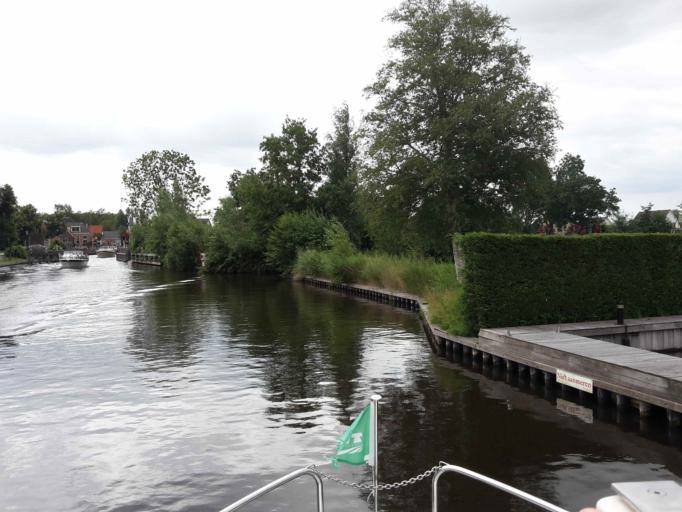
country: NL
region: Overijssel
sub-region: Gemeente Steenwijkerland
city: Oldemarkt
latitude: 52.8099
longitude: 5.9183
